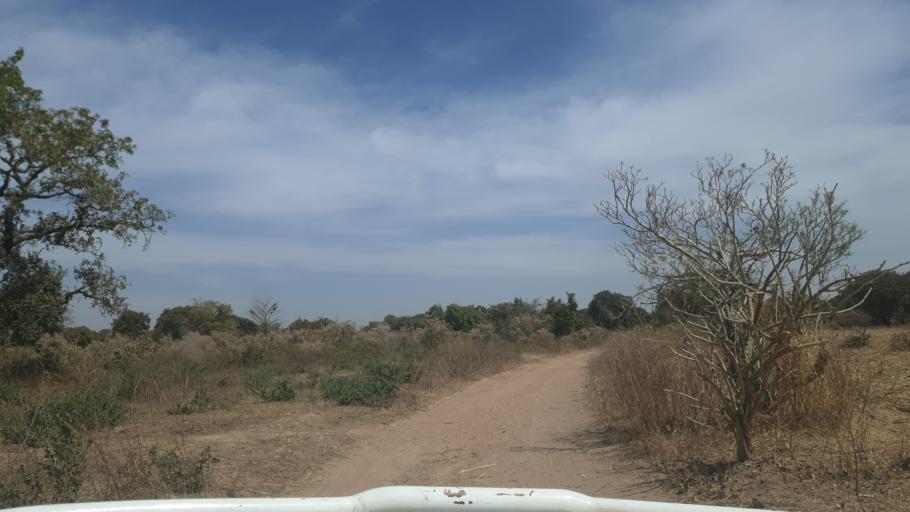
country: ML
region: Sikasso
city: Yorosso
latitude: 12.2839
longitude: -4.6829
